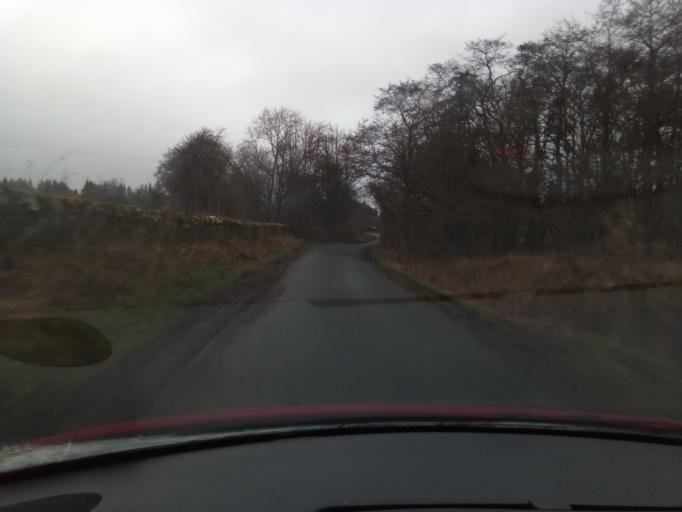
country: GB
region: Scotland
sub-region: The Scottish Borders
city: Kelso
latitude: 55.5505
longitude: -2.4321
